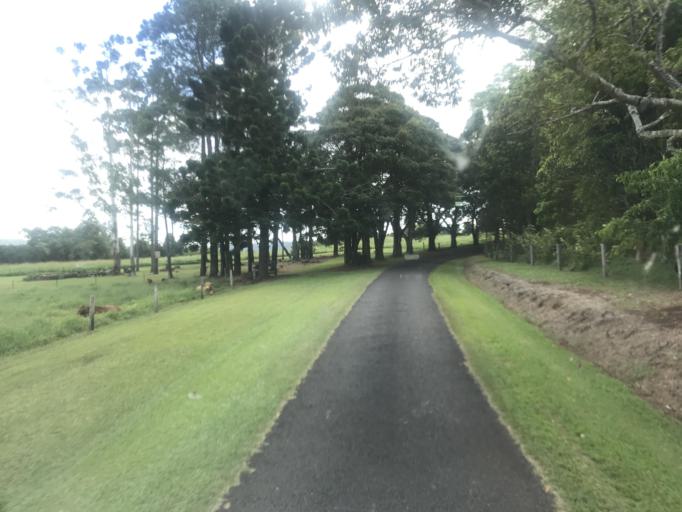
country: AU
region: Queensland
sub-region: Tablelands
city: Ravenshoe
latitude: -17.5540
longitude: 145.6941
